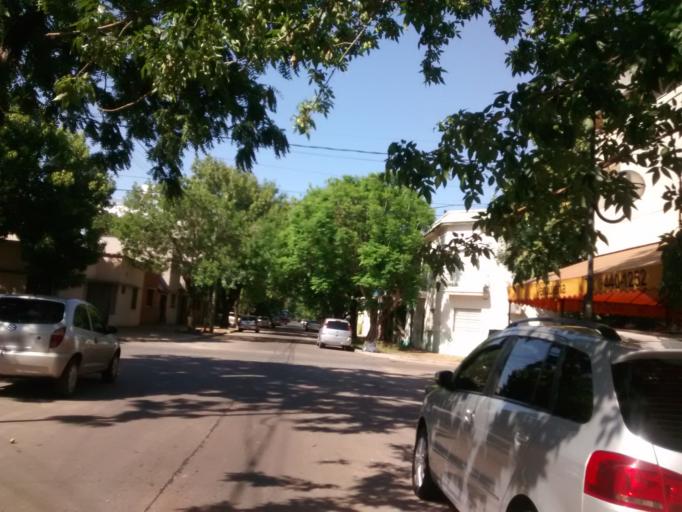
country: AR
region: Buenos Aires
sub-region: Partido de La Plata
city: La Plata
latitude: -34.8996
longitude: -57.9637
